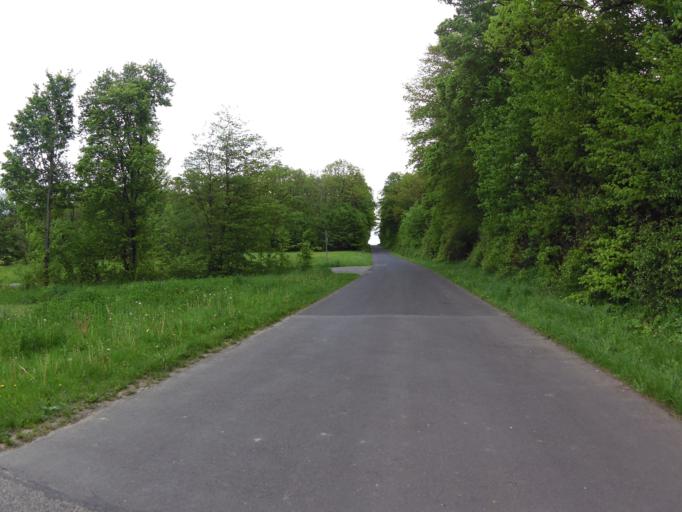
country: DE
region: Bavaria
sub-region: Regierungsbezirk Unterfranken
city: Unterpleichfeld
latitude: 49.8444
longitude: 10.0669
